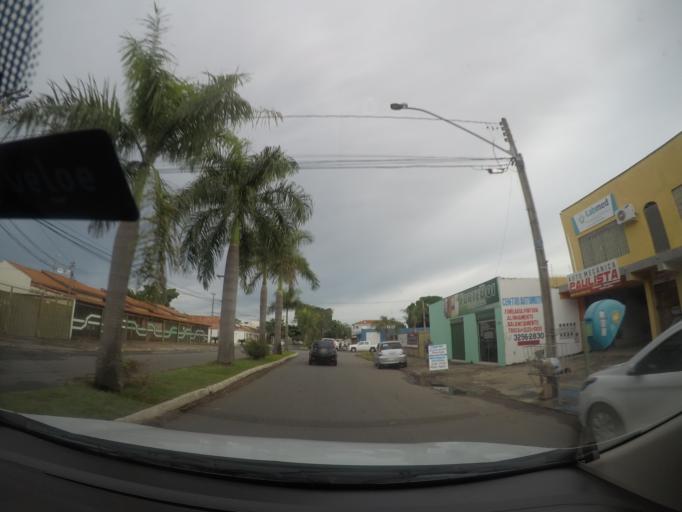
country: BR
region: Goias
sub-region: Goiania
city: Goiania
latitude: -16.7125
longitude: -49.3108
